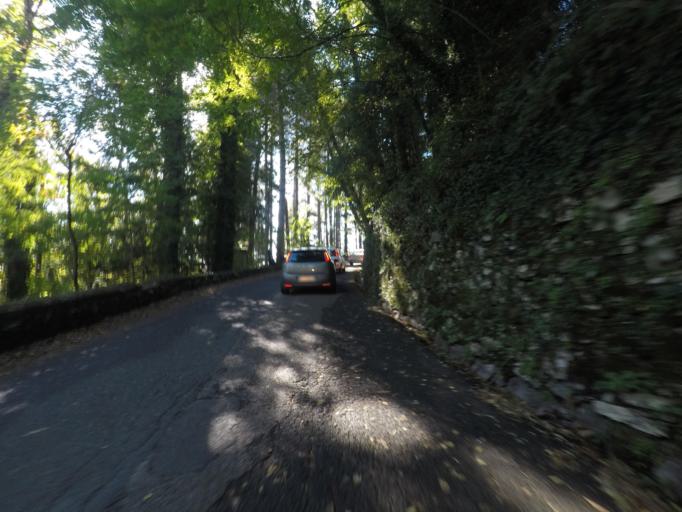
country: IT
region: Liguria
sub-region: Provincia di La Spezia
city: Casano-Dogana-Isola
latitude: 44.1105
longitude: 10.0768
